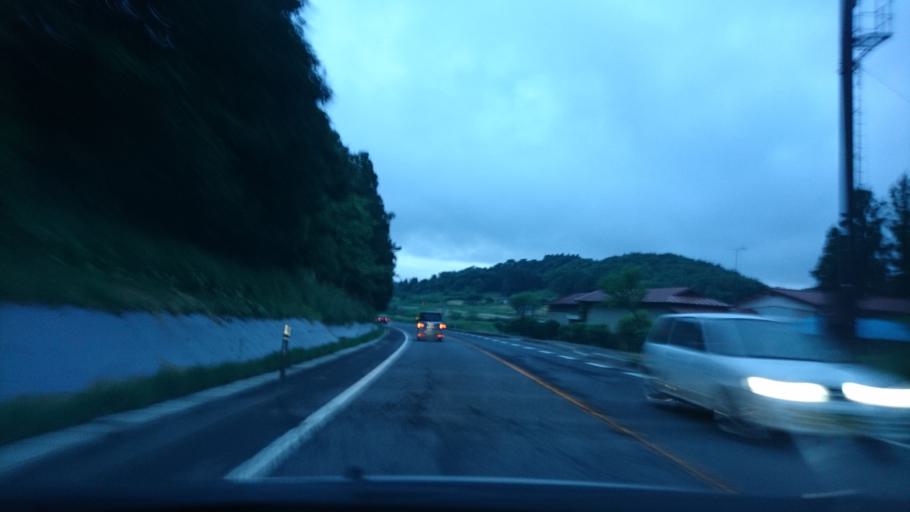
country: JP
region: Iwate
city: Ichinoseki
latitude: 38.8328
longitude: 141.0836
